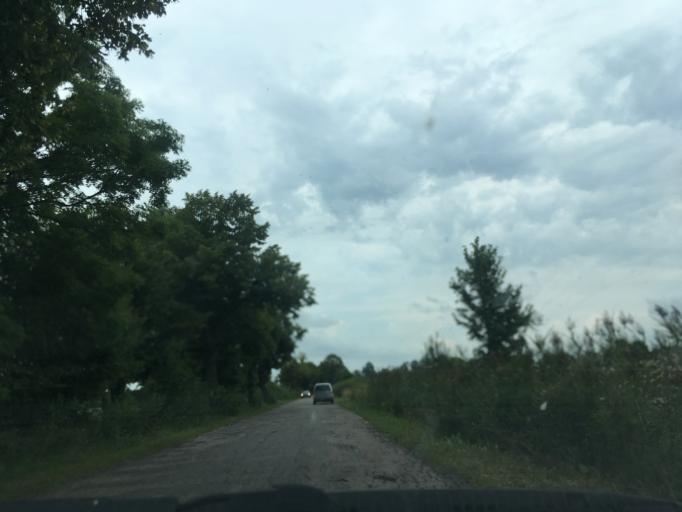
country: PL
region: Warmian-Masurian Voivodeship
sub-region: Powiat wegorzewski
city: Pozezdrze
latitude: 54.1418
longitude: 21.7779
